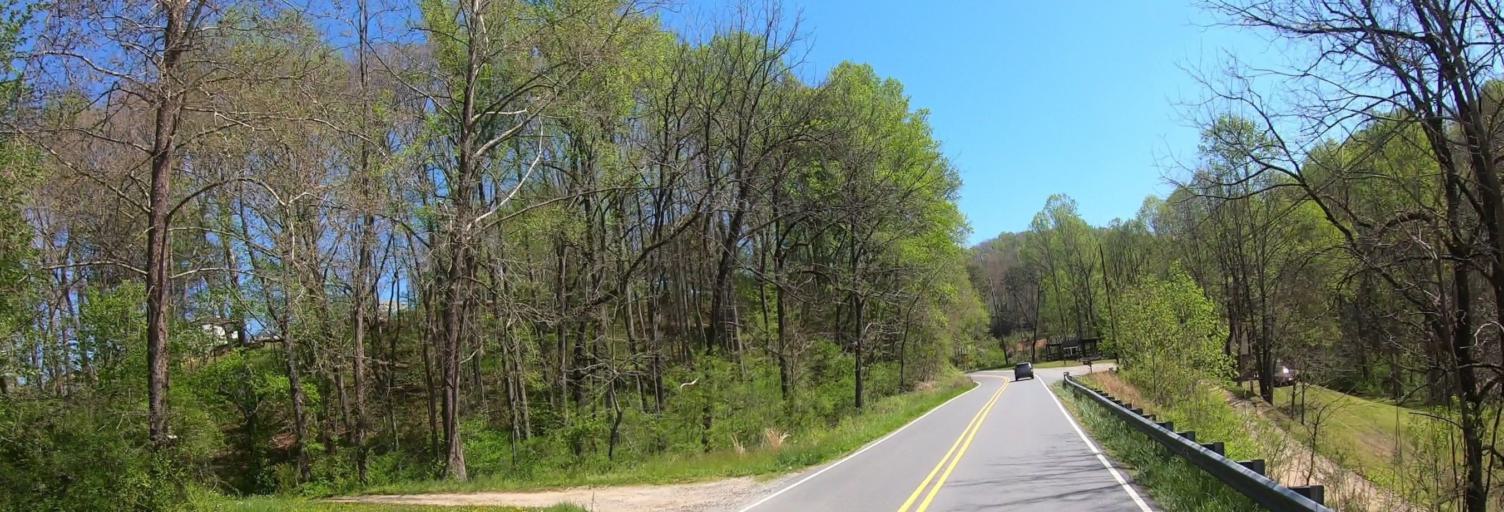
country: US
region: North Carolina
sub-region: Swain County
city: Cherokee
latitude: 35.4476
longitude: -83.3785
